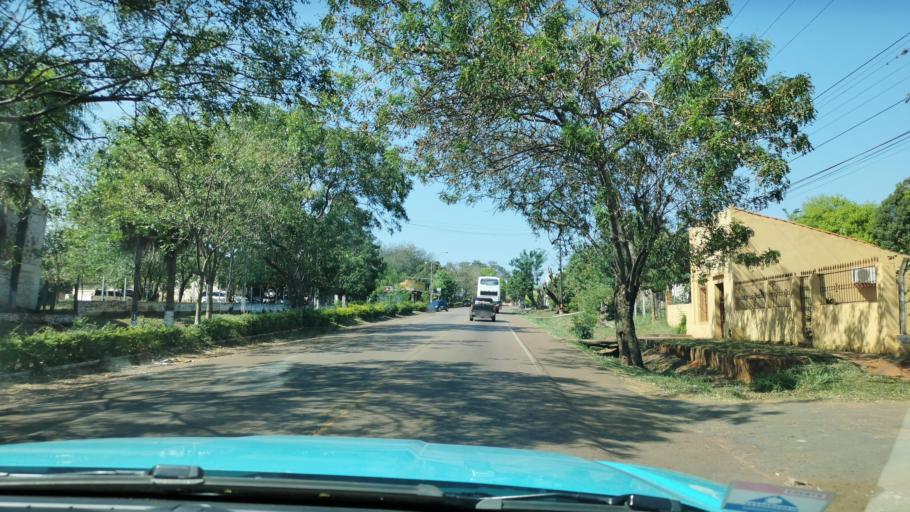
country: PY
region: Paraguari
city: Quiindy
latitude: -25.8765
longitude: -57.2897
